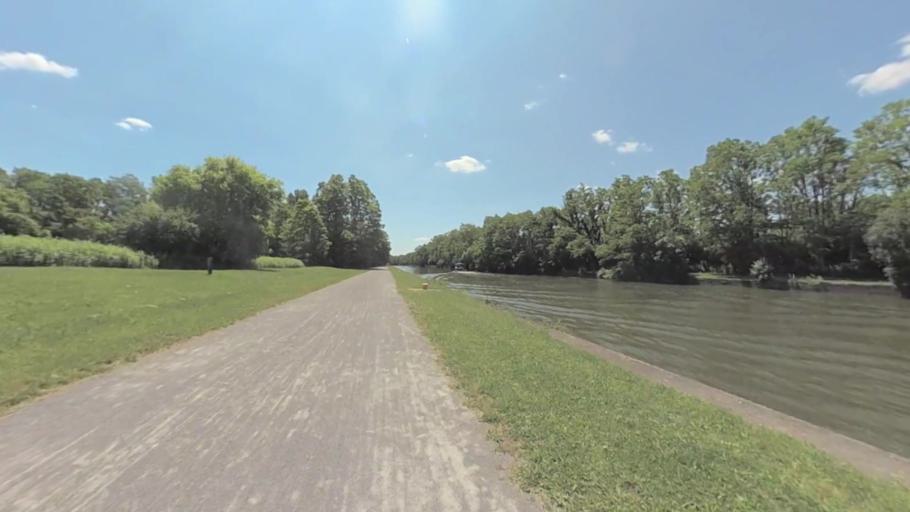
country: US
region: New York
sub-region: Monroe County
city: Pittsford
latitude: 43.0705
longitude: -77.4907
